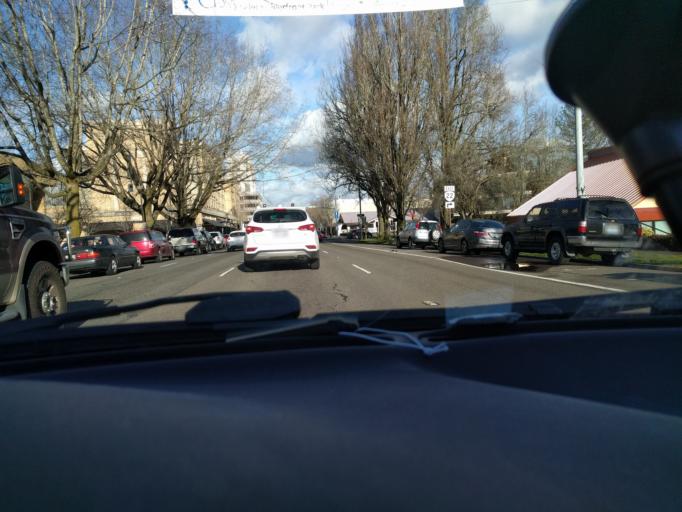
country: US
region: Oregon
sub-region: Marion County
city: Salem
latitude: 44.9373
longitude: -123.0403
